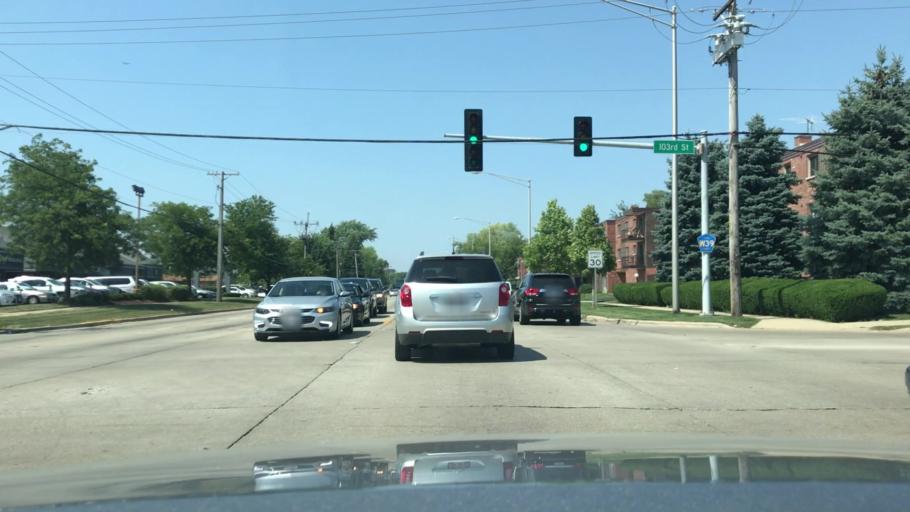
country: US
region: Illinois
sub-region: Cook County
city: Oak Lawn
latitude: 41.7051
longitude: -87.7598
